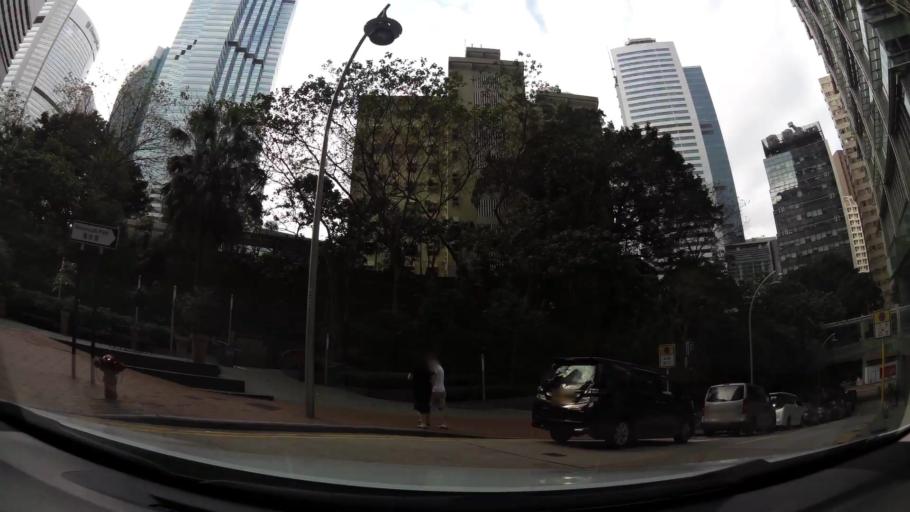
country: HK
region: Wanchai
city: Wan Chai
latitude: 22.2768
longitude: 114.1673
